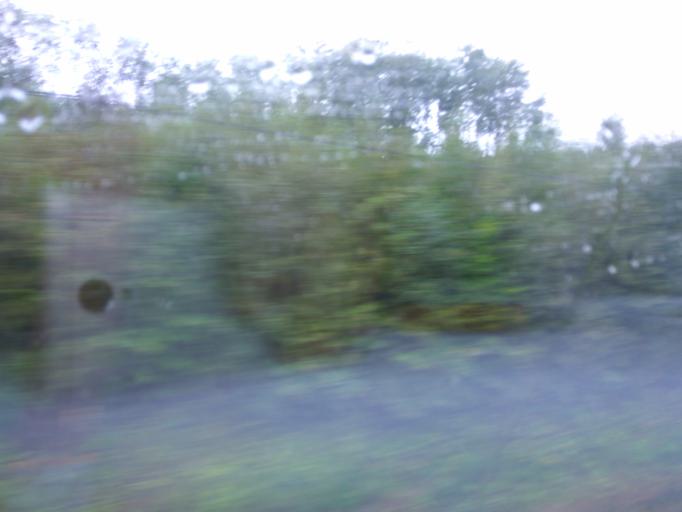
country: RU
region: Moskovskaya
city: Zhilevo
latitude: 55.0205
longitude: 38.0130
